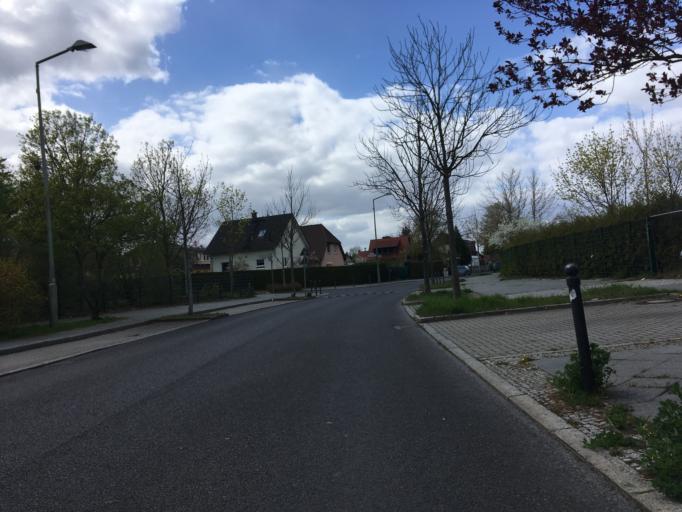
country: DE
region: Berlin
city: Altglienicke
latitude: 52.4077
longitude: 13.5370
